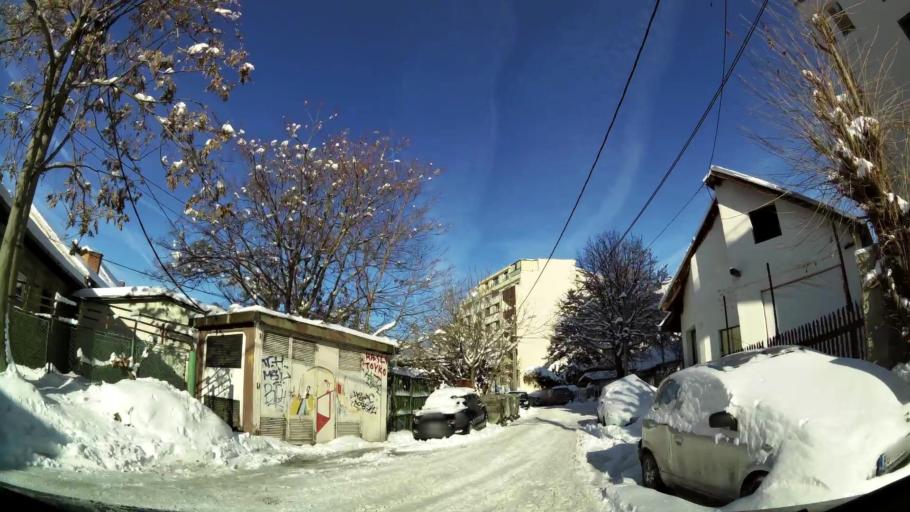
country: RS
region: Central Serbia
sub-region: Belgrade
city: Vracar
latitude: 44.7889
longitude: 20.4908
